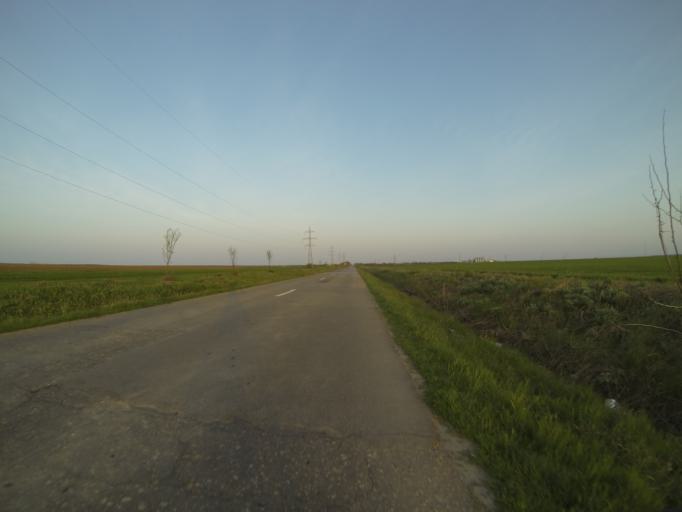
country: RO
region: Dolj
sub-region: Comuna Dranicu
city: Dranic
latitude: 44.0621
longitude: 23.8201
